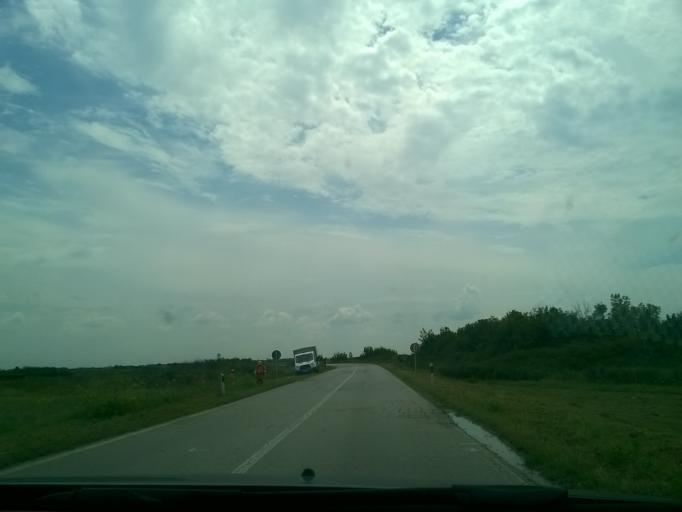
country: RS
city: Konak
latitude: 45.2977
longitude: 20.9266
